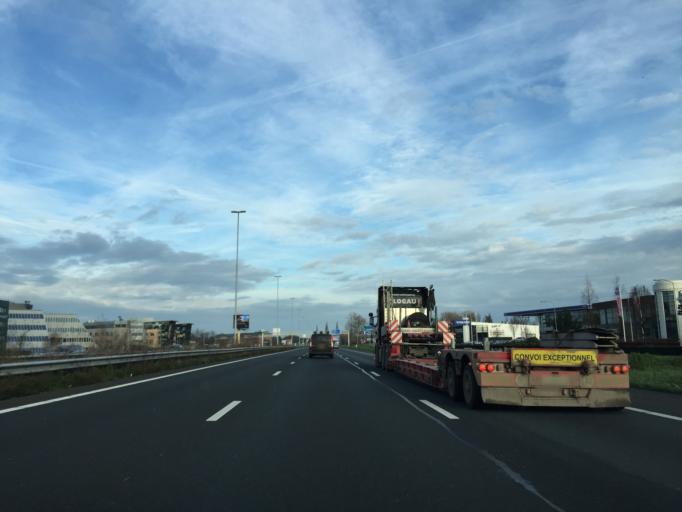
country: NL
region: Gelderland
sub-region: Gemeente Zaltbommel
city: Zaltbommel
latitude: 51.7978
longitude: 5.2585
